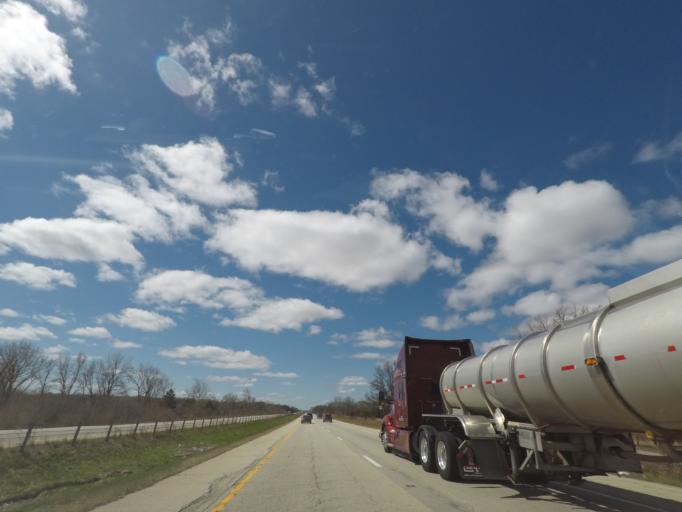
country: US
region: Illinois
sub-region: Grundy County
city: Central City
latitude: 41.2212
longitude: -88.2832
